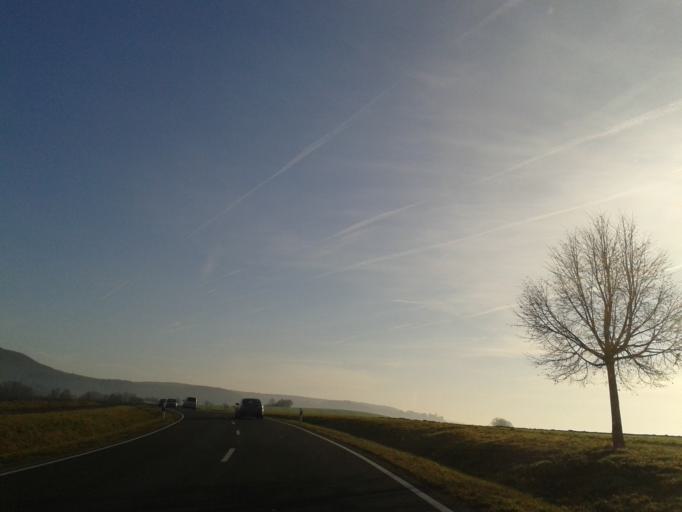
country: DE
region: Bavaria
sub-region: Regierungsbezirk Unterfranken
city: Hofheim in Unterfranken
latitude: 50.0996
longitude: 10.5472
